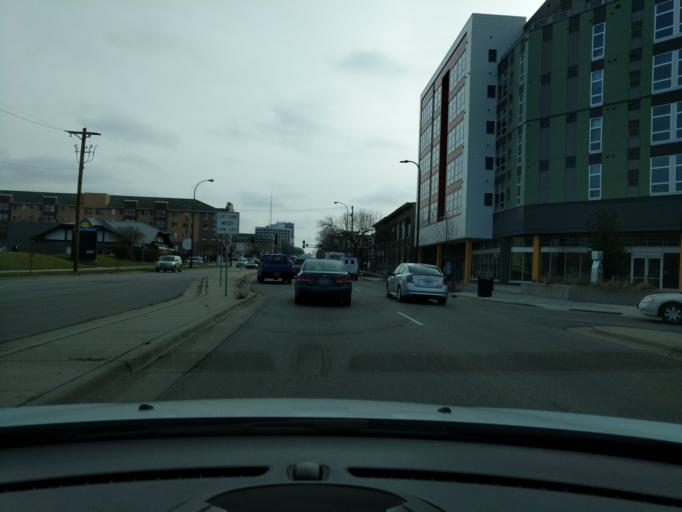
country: US
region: Minnesota
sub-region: Ramsey County
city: Lauderdale
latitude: 44.9739
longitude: -93.2228
